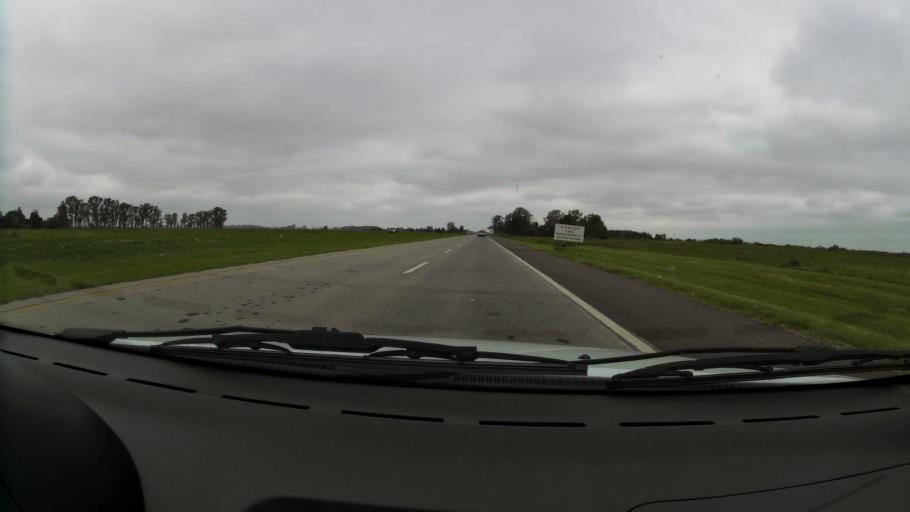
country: AR
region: Buenos Aires
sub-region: Partido de Brandsen
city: Brandsen
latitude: -35.0334
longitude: -58.1974
